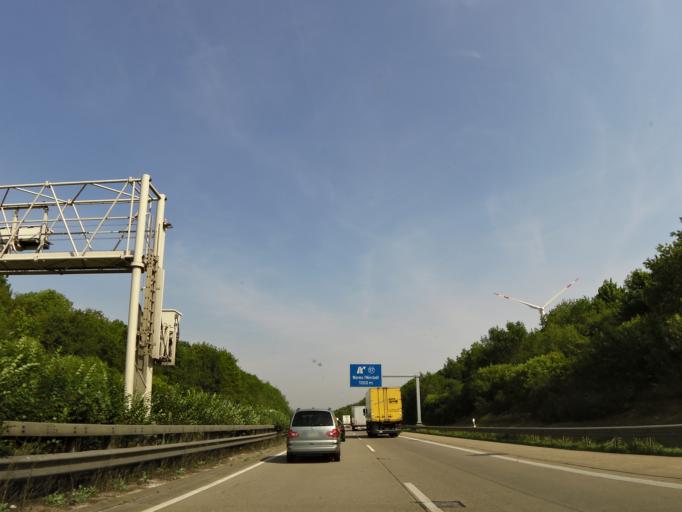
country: DE
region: Rheinland-Pfalz
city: Morstadt
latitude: 49.6534
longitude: 8.2874
